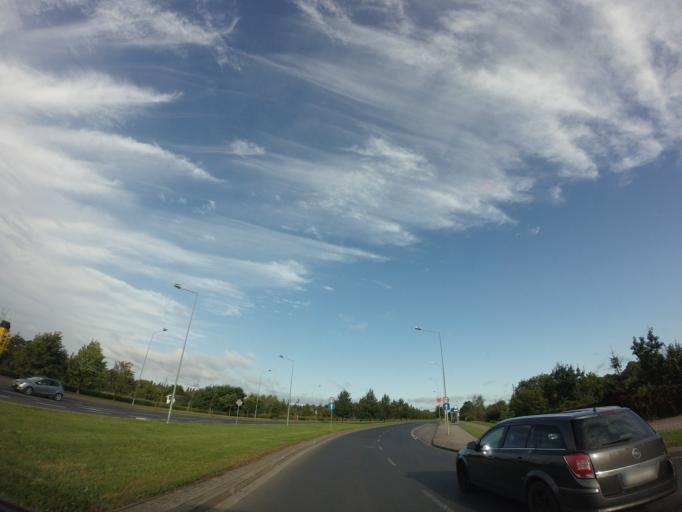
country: PL
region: West Pomeranian Voivodeship
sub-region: Szczecin
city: Szczecin
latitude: 53.4291
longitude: 14.4996
